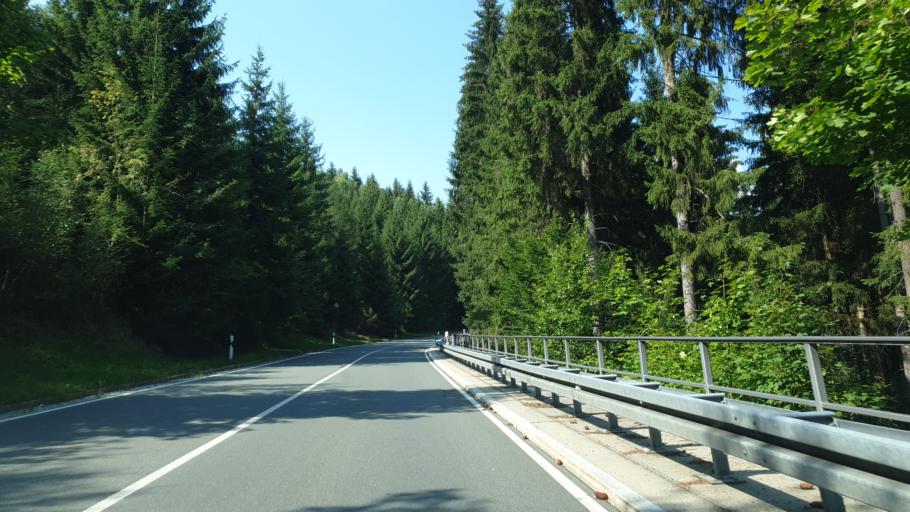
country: DE
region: Saxony
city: Zwota
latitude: 50.3579
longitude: 12.4208
